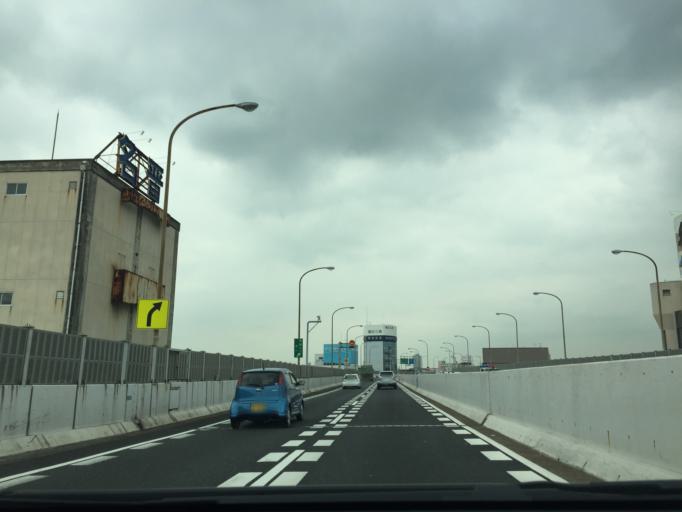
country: JP
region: Aichi
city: Nagoya-shi
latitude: 35.1031
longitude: 136.9245
